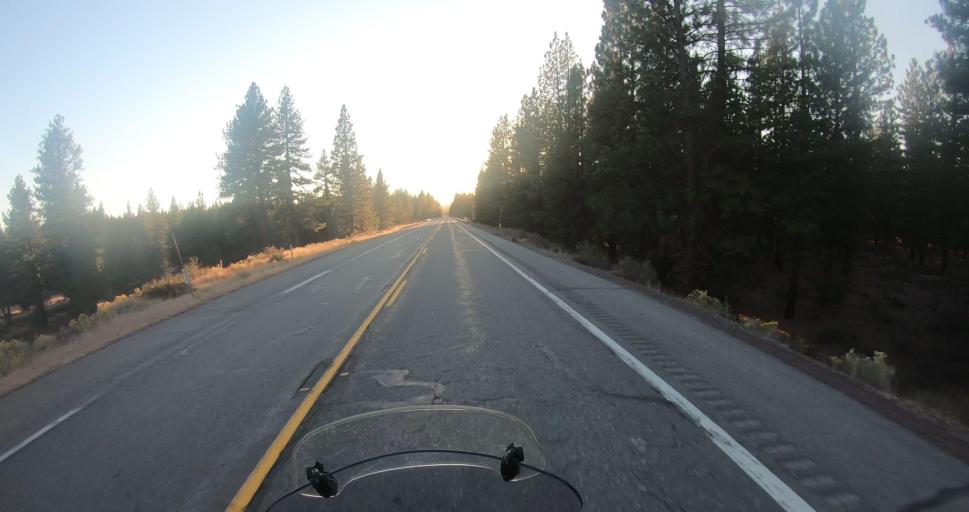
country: US
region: California
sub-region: Lassen County
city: Susanville
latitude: 40.4145
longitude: -120.7402
